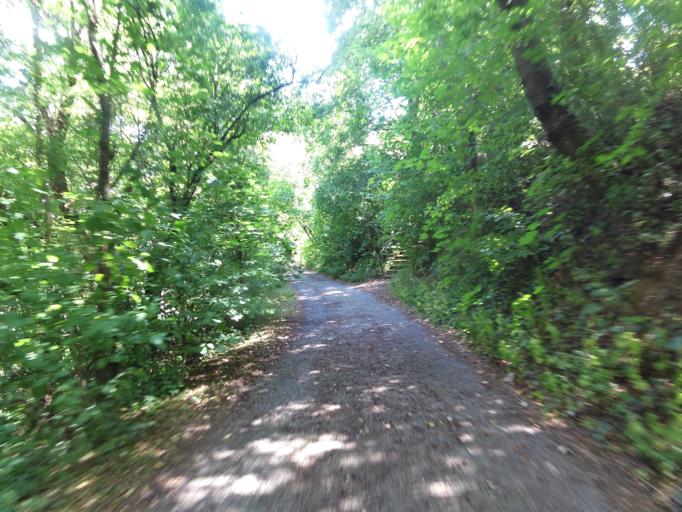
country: DE
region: Bavaria
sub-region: Regierungsbezirk Unterfranken
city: Wuerzburg
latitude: 49.8131
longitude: 9.9586
